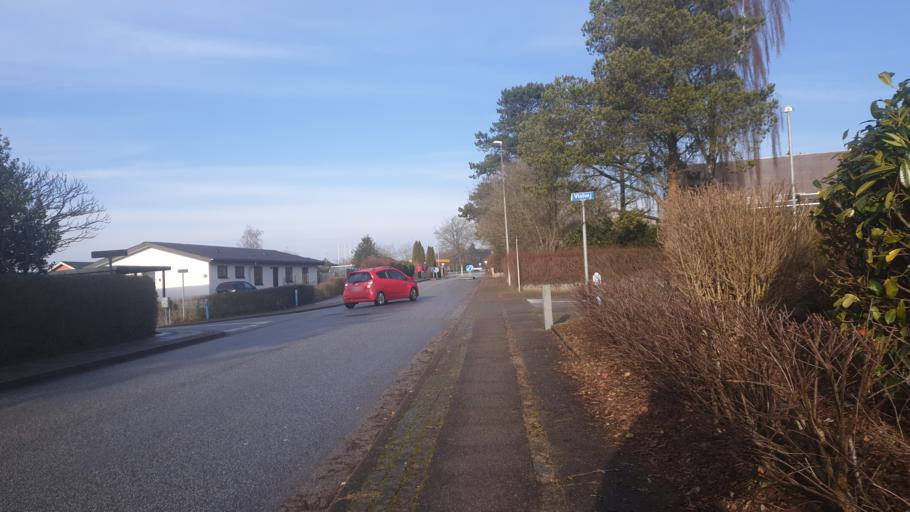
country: DK
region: Central Jutland
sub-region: Hedensted Kommune
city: Hedensted
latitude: 55.7762
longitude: 9.7147
